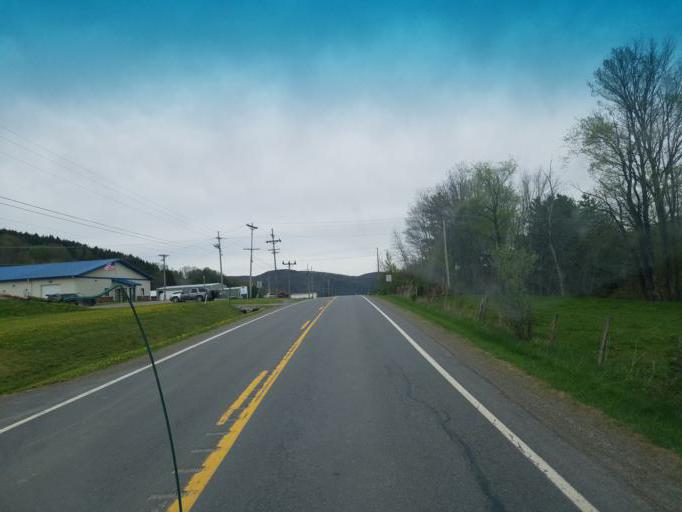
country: US
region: Pennsylvania
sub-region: Tioga County
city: Westfield
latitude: 41.8962
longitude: -77.5327
